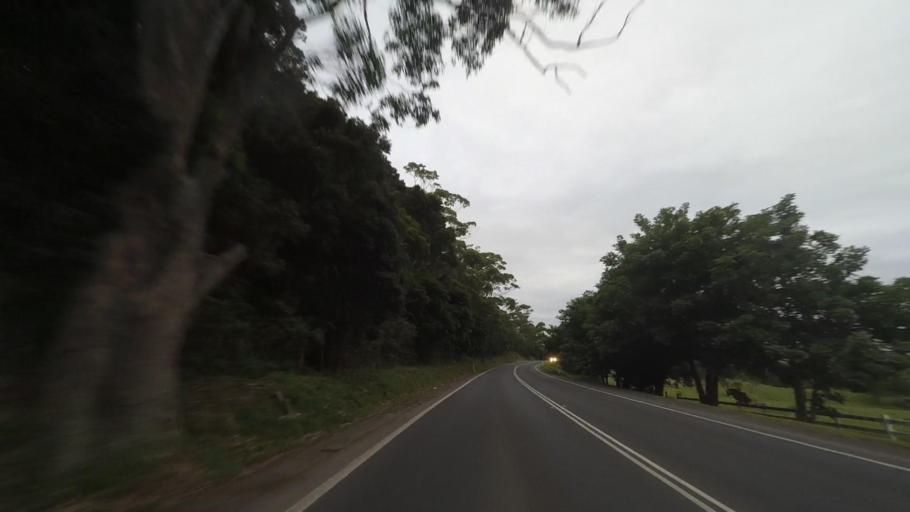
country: AU
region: New South Wales
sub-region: Kiama
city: Gerringong
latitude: -34.7426
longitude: 150.7720
